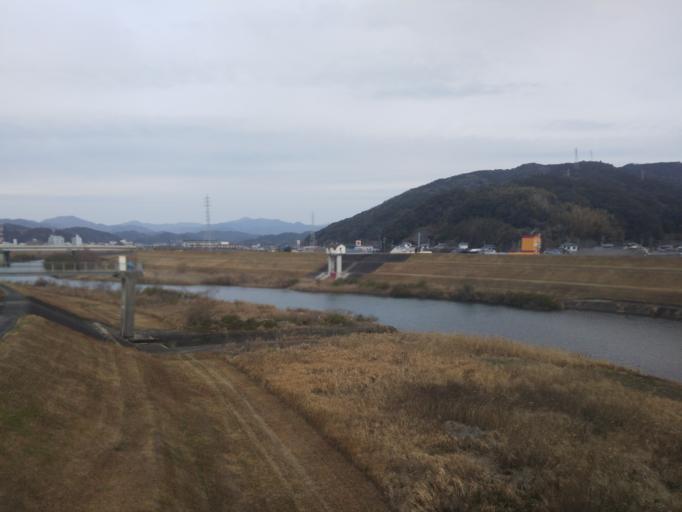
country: JP
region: Kochi
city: Nakamura
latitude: 32.9802
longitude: 132.9510
